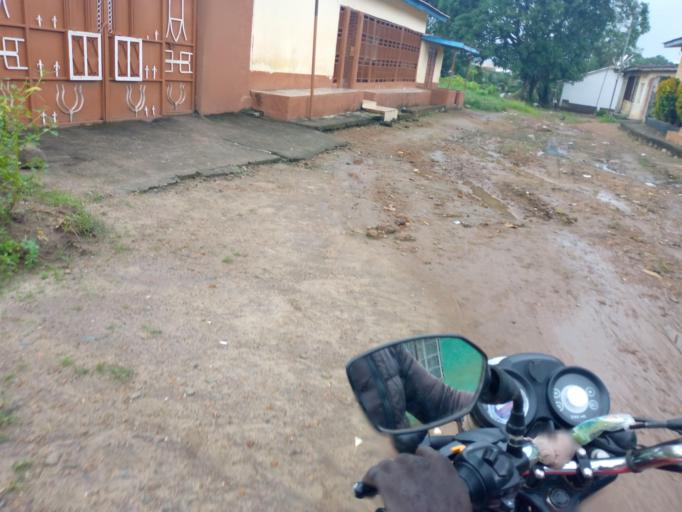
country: SL
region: Eastern Province
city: Kenema
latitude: 7.8831
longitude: -11.1790
